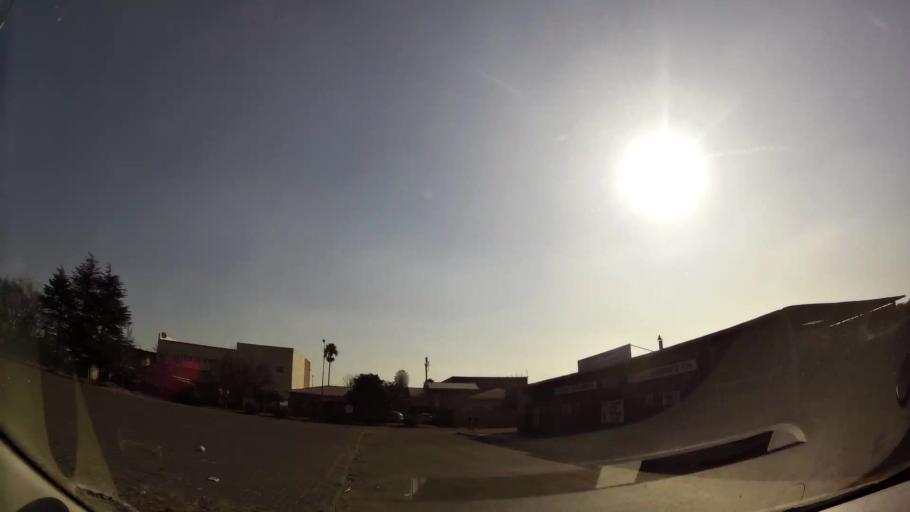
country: ZA
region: Gauteng
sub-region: West Rand District Municipality
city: Randfontein
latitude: -26.1811
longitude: 27.7055
